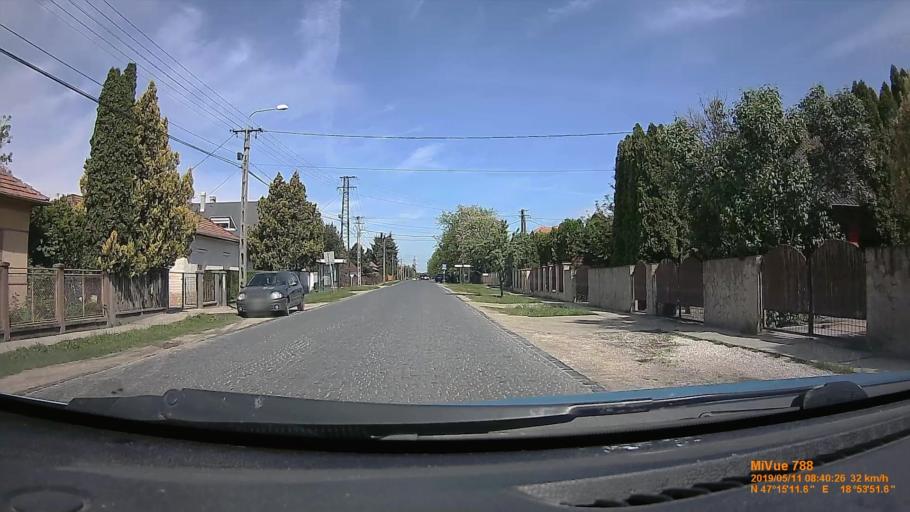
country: HU
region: Fejer
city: Ercsi
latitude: 47.2534
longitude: 18.8976
